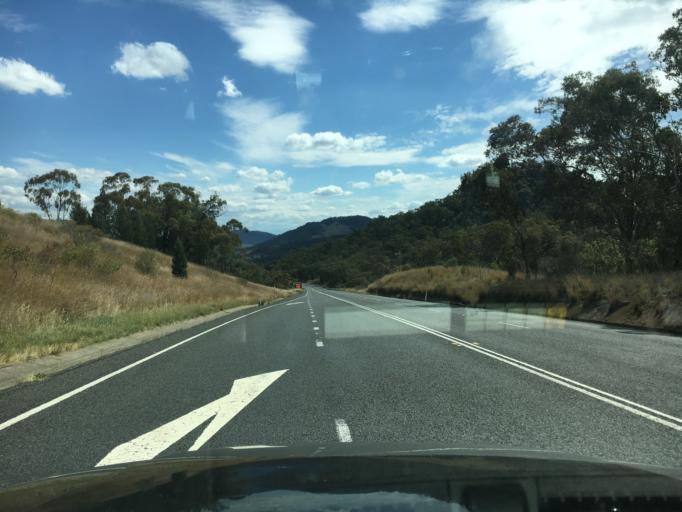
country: AU
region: New South Wales
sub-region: Liverpool Plains
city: Quirindi
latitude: -31.4438
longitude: 150.8772
